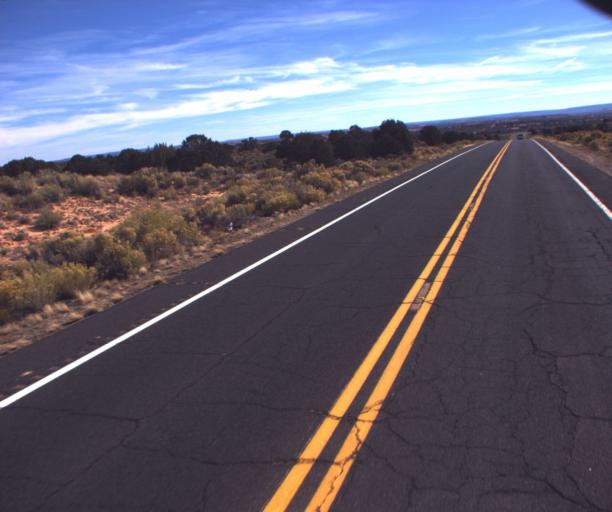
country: US
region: Arizona
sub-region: Coconino County
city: Kaibito
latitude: 36.5799
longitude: -110.7908
